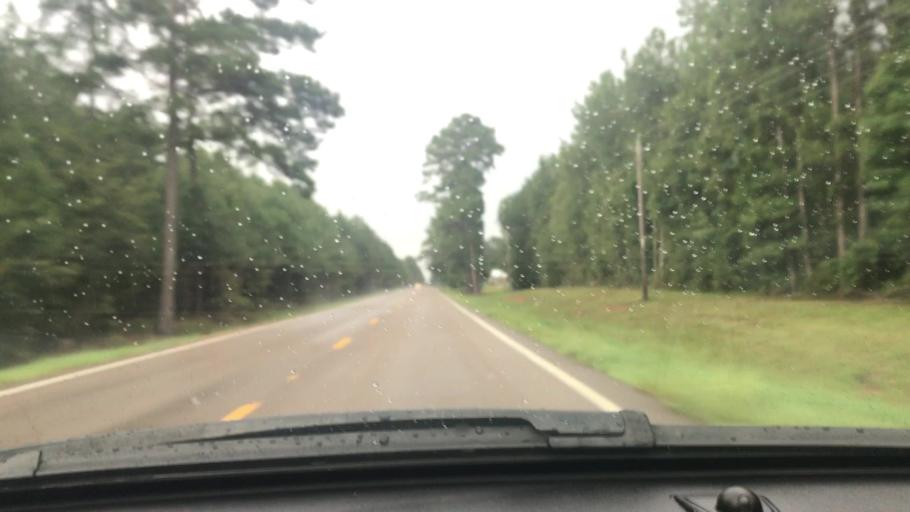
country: US
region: Mississippi
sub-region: Pike County
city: Summit
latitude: 31.3445
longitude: -90.5880
